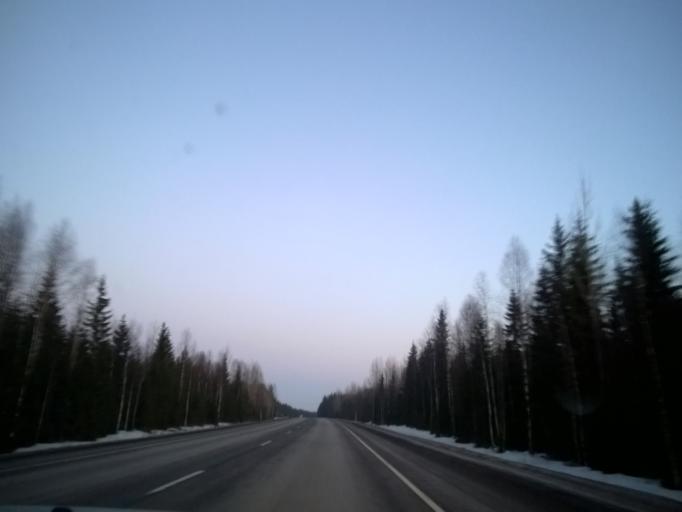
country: FI
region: Northern Ostrobothnia
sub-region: Nivala-Haapajaervi
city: Pyhaesalmi
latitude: 63.7861
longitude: 25.9268
